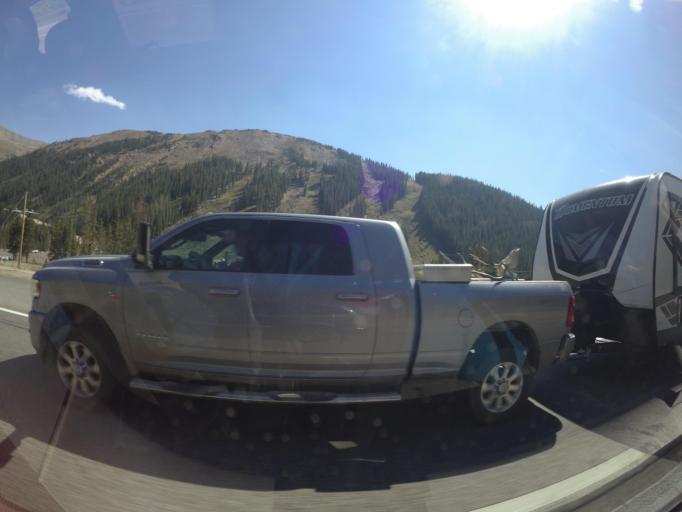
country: US
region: Colorado
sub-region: Summit County
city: Keystone
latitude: 39.6820
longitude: -105.8983
